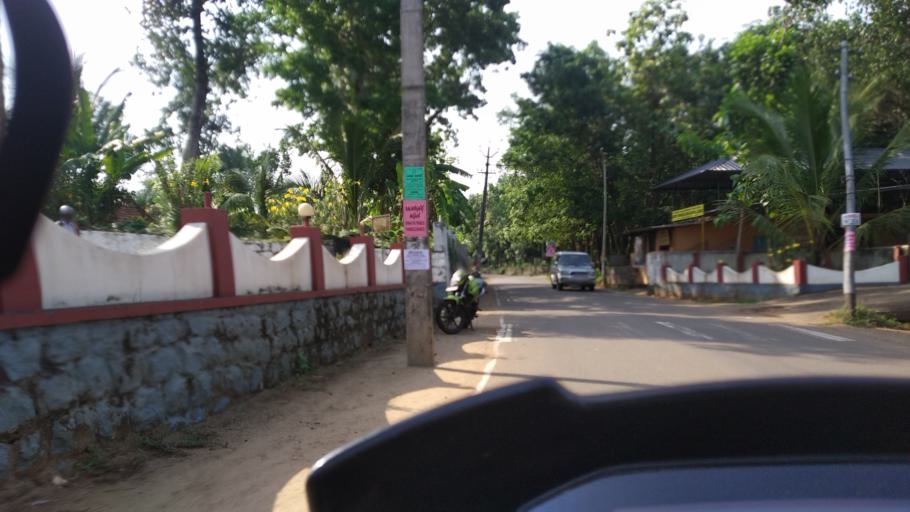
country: IN
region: Kerala
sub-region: Ernakulam
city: Piravam
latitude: 9.8329
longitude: 76.5430
